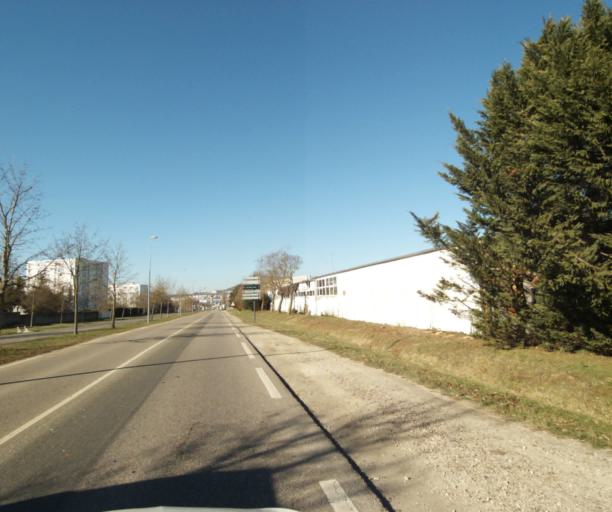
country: FR
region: Lorraine
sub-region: Departement de Meurthe-et-Moselle
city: Tomblaine
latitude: 48.6873
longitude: 6.2172
